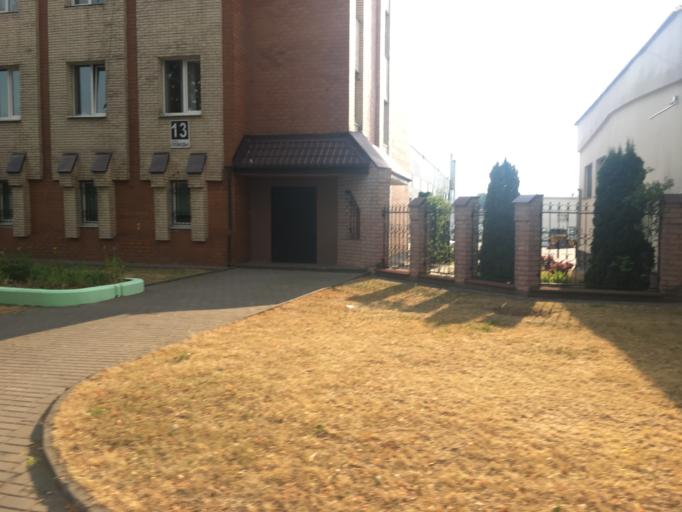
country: BY
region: Grodnenskaya
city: Hrodna
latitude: 53.6605
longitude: 23.8300
